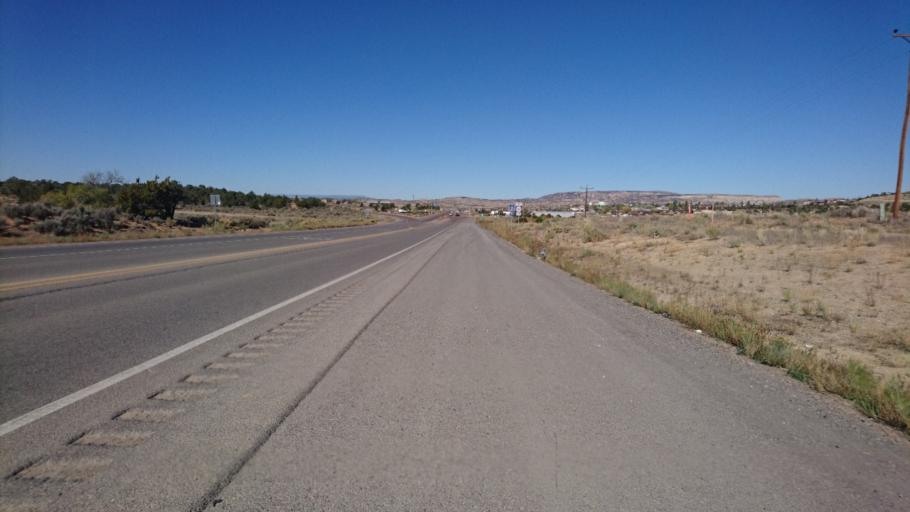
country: US
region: New Mexico
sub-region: McKinley County
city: Gallup
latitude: 35.4995
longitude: -108.7398
